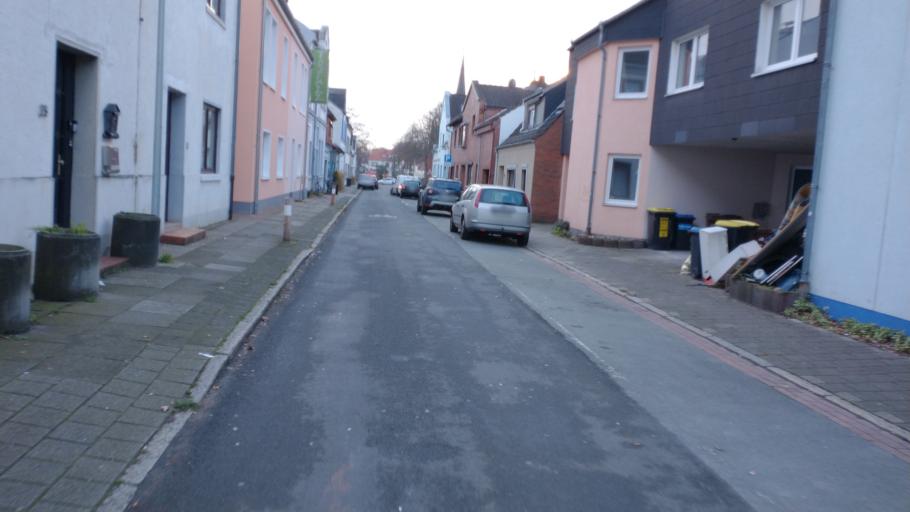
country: DE
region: Lower Saxony
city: Lilienthal
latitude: 53.0572
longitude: 8.8890
